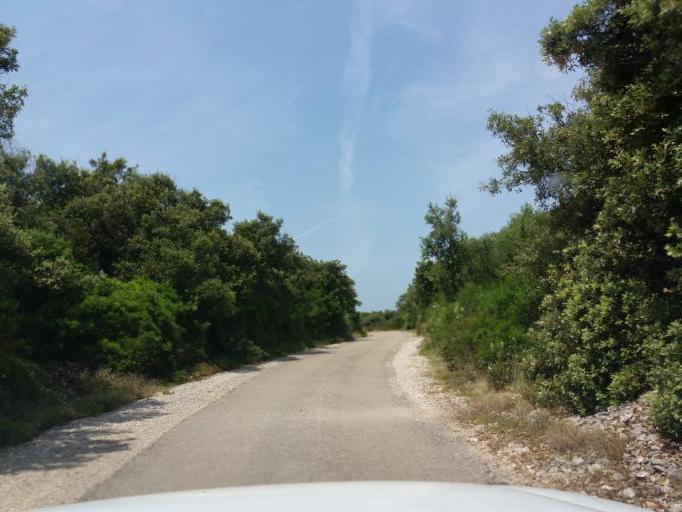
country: HR
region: Zadarska
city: Ugljan
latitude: 44.1437
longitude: 14.8409
